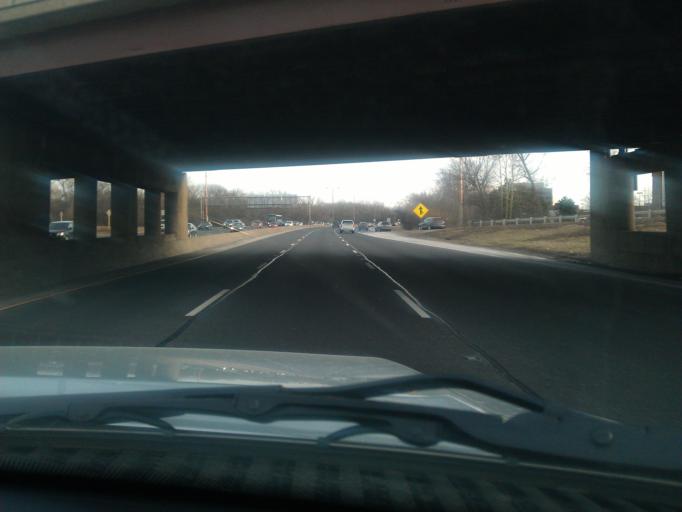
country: US
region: Illinois
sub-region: Cook County
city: Glencoe
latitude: 42.1383
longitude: -87.7886
